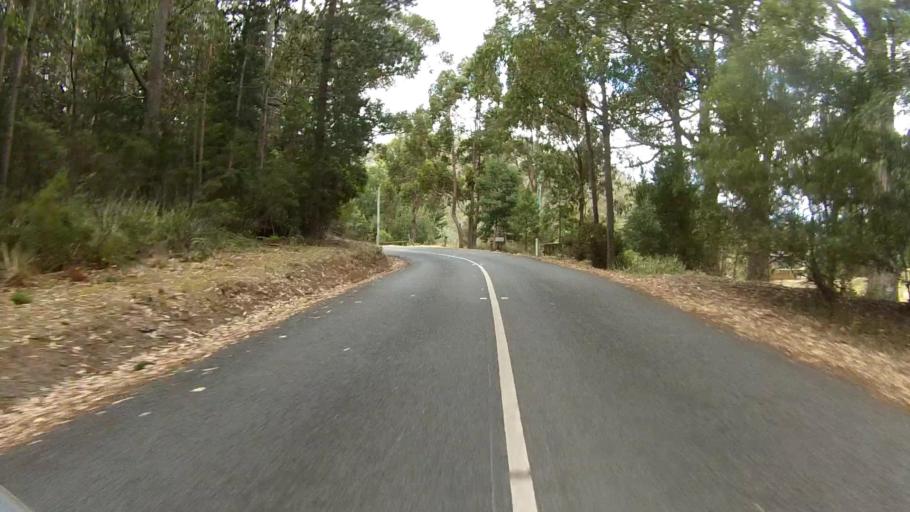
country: AU
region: Tasmania
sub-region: Kingborough
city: Margate
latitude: -42.9743
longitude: 147.1717
